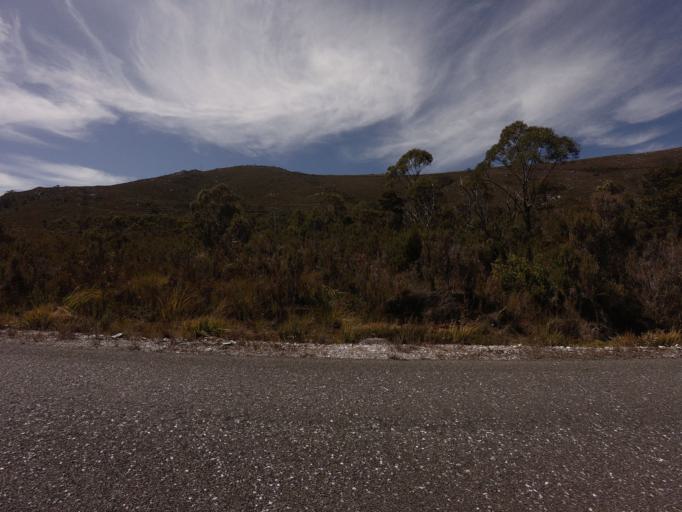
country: AU
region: Tasmania
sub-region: West Coast
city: Queenstown
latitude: -42.7844
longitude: 146.0613
